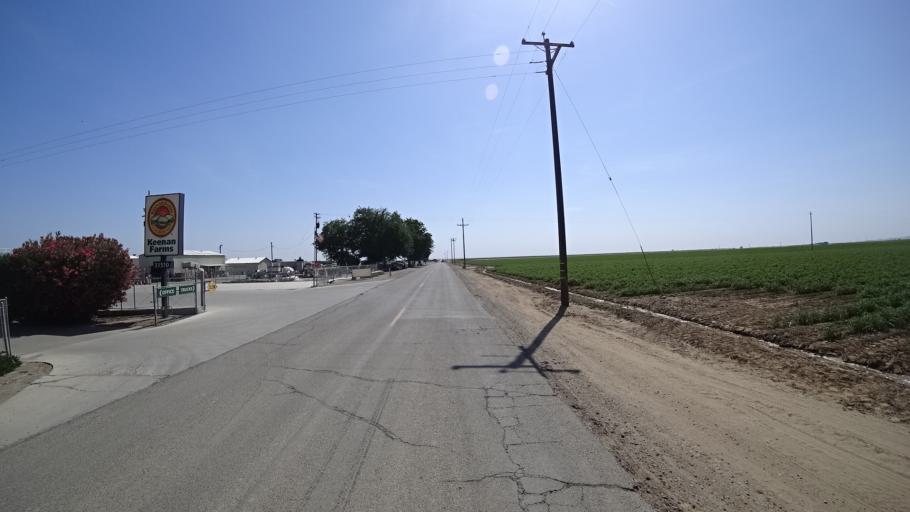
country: US
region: California
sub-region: Kings County
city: Kettleman City
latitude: 36.0725
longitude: -120.0314
